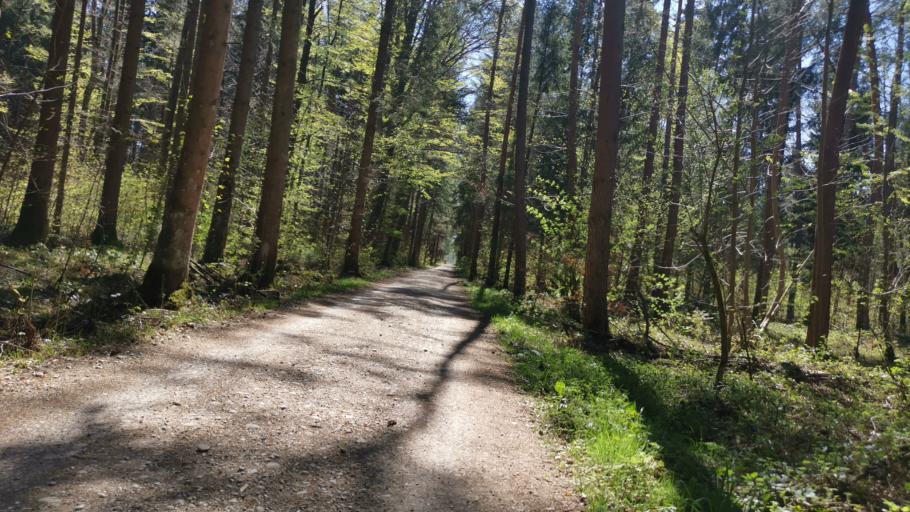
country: DE
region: Bavaria
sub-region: Upper Bavaria
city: Planegg
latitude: 48.0830
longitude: 11.4261
